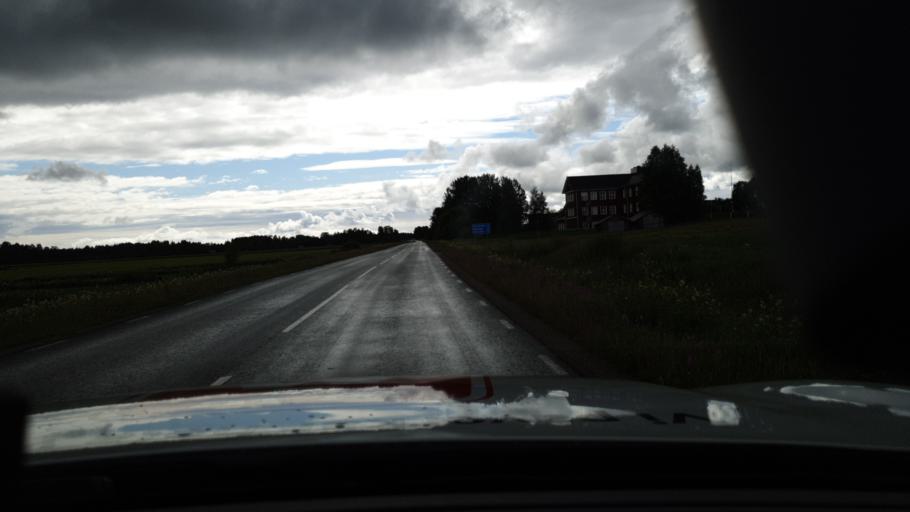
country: SE
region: Norrbotten
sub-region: Pitea Kommun
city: Rosvik
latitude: 65.5308
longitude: 21.7972
